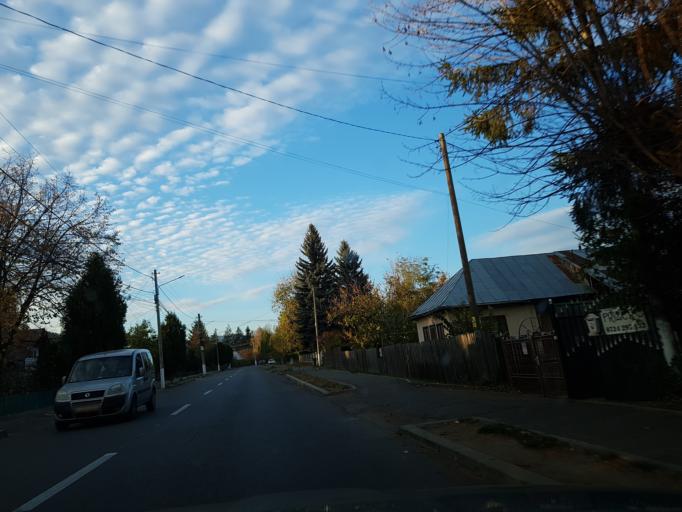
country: RO
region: Prahova
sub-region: Oras Breaza
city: Breaza de Sus
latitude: 45.1922
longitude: 25.6582
